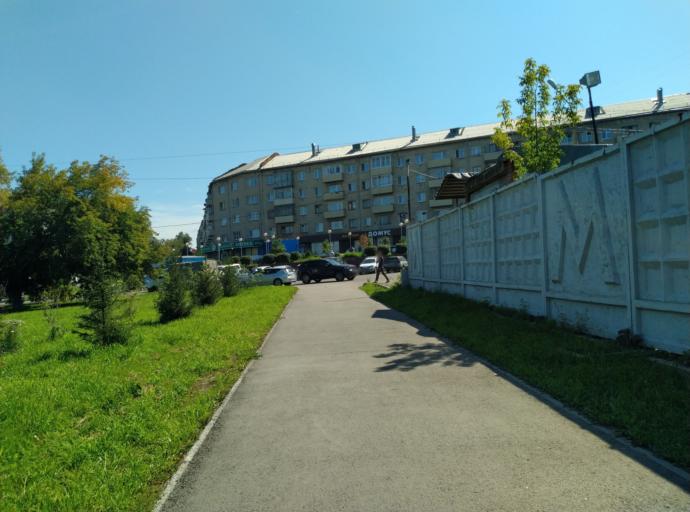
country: RU
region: Krasnoyarskiy
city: Krasnoyarsk
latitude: 56.0275
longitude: 92.7785
